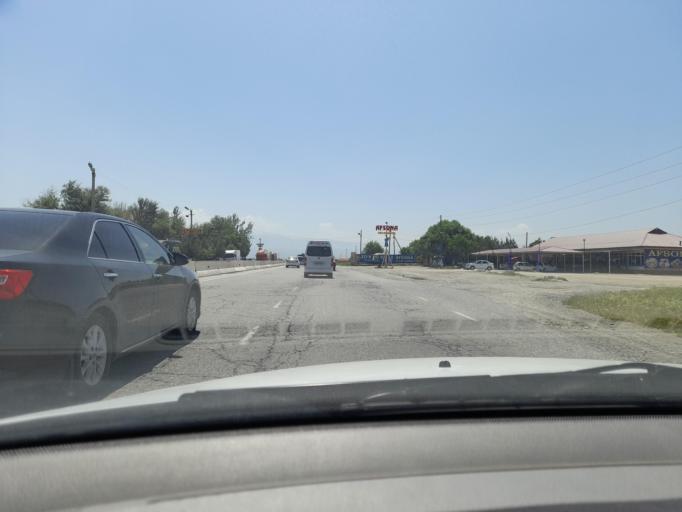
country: UZ
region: Jizzax
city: Jizzax
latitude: 40.1604
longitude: 67.9590
